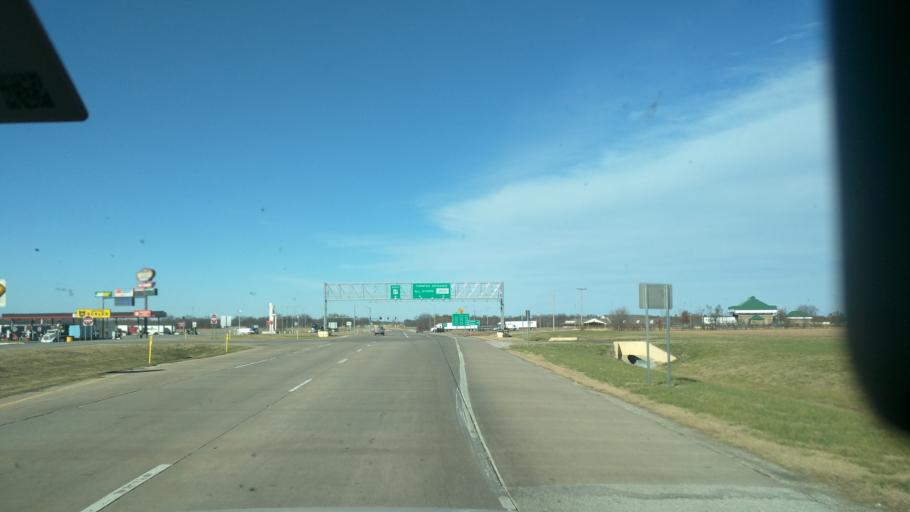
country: US
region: Oklahoma
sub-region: Craig County
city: Vinita
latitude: 36.5643
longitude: -95.2200
